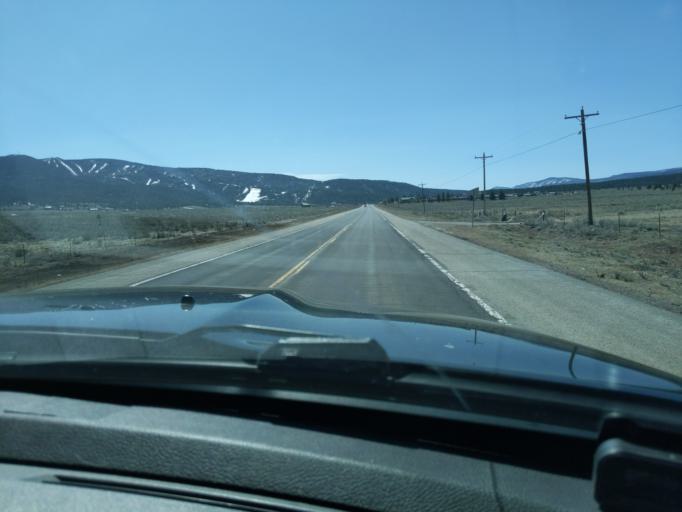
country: US
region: New Mexico
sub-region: Colfax County
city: Angel Fire
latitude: 36.4181
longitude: -105.2958
